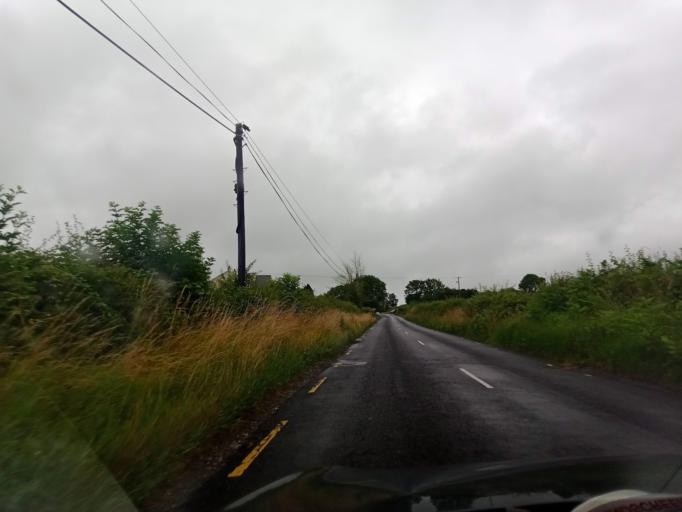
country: IE
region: Leinster
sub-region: Laois
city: Abbeyleix
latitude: 52.9101
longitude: -7.3091
